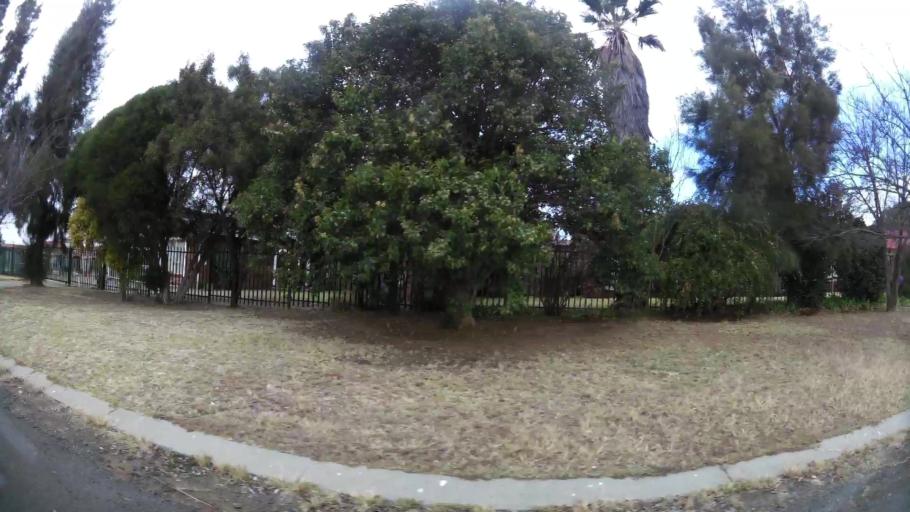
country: ZA
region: Orange Free State
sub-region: Fezile Dabi District Municipality
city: Kroonstad
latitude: -27.6308
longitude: 27.2444
